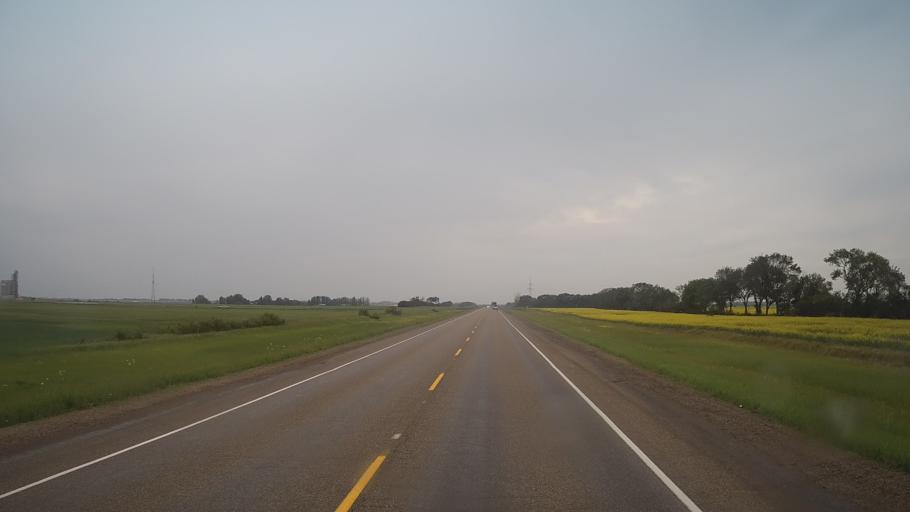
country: CA
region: Saskatchewan
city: Saskatoon
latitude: 52.1292
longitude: -106.8405
